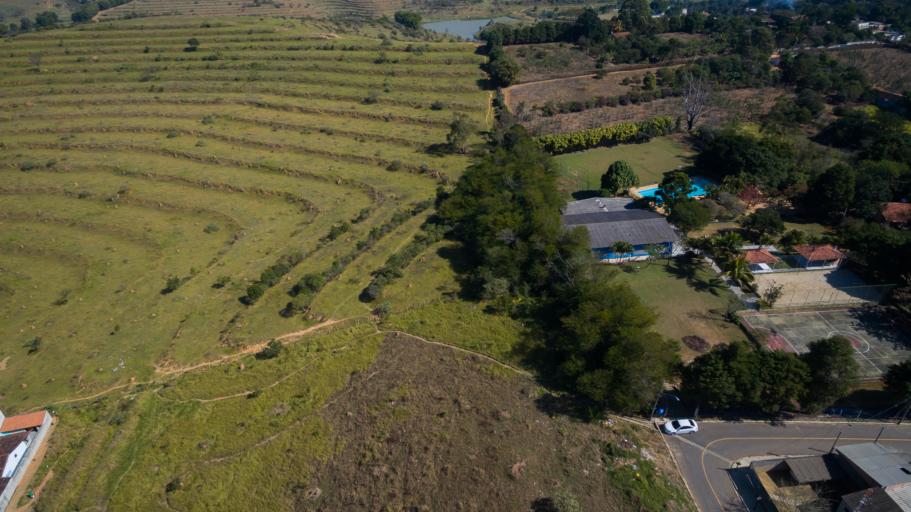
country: BR
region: Sao Paulo
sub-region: Sao Jose Dos Campos
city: Sao Jose dos Campos
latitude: -23.2252
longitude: -45.7966
